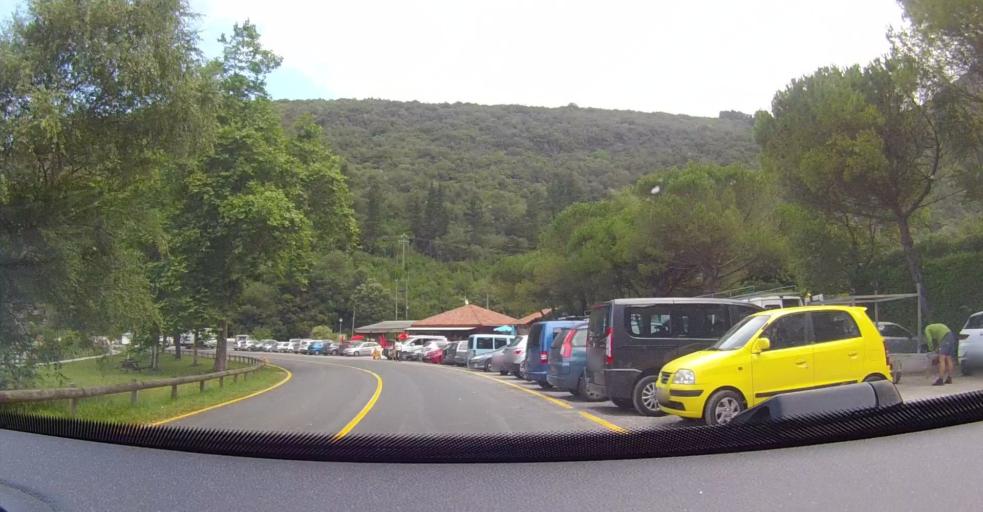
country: ES
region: Basque Country
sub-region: Bizkaia
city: Mundaka
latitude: 43.3947
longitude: -2.6807
